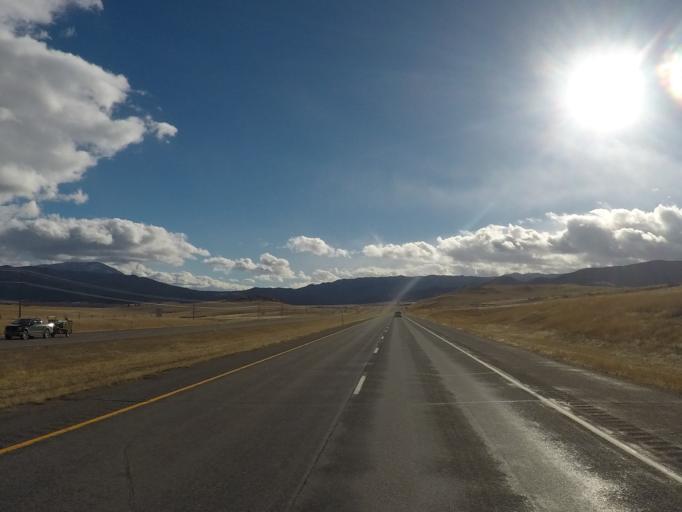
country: US
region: Montana
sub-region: Jefferson County
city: Boulder
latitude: 46.2606
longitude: -112.1103
